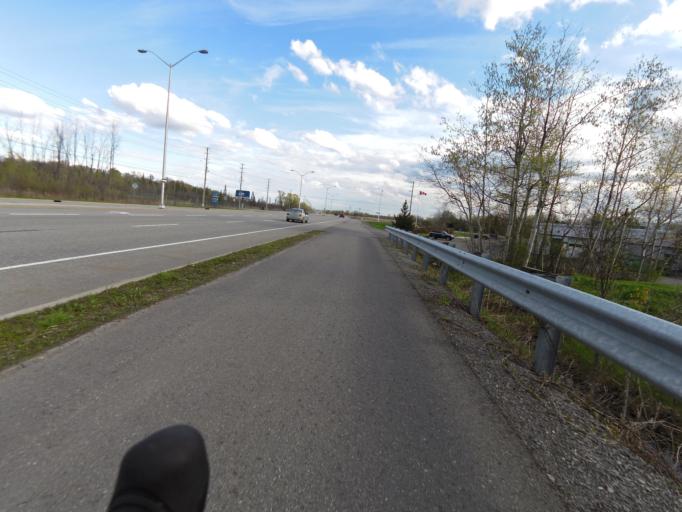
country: CA
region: Ontario
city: Ottawa
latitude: 45.3167
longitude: -75.6872
